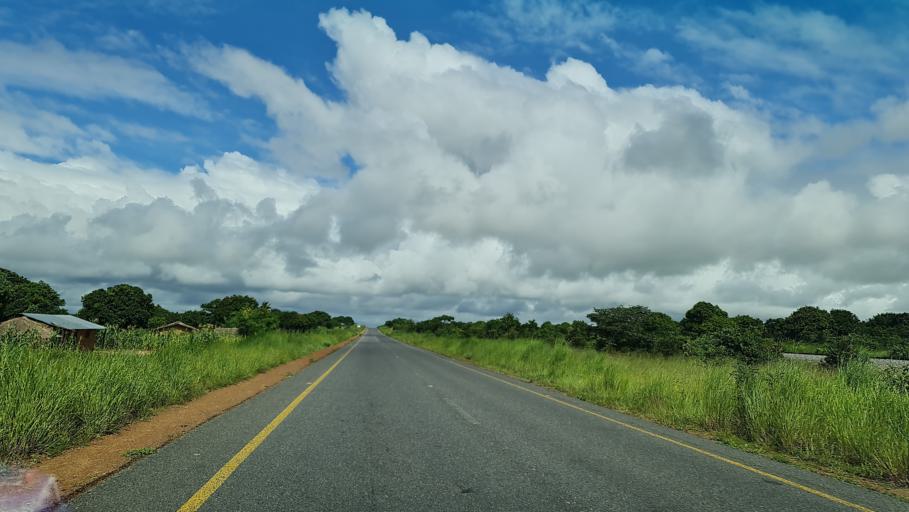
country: MZ
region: Nampula
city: Nampula
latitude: -15.0234
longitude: 38.4821
